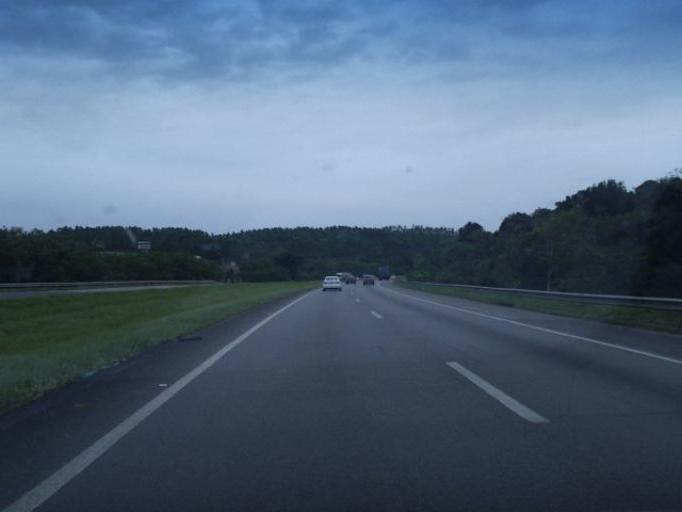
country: BR
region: Sao Paulo
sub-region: Registro
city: Registro
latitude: -24.5626
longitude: -47.8684
